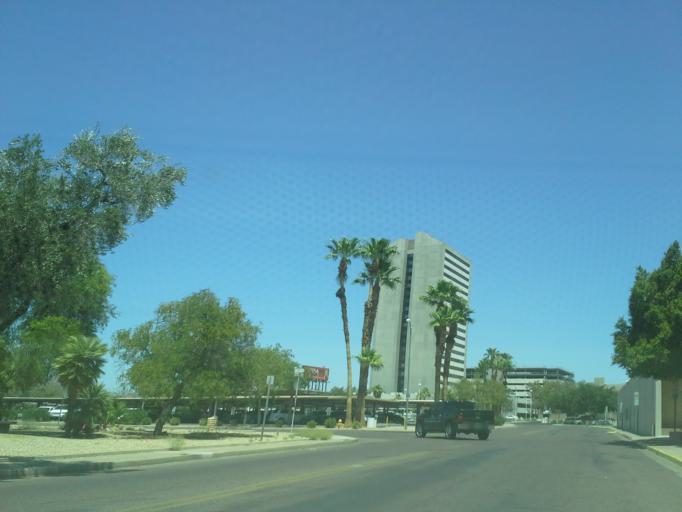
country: US
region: Arizona
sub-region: Maricopa County
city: Phoenix
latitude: 33.4929
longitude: -112.0764
